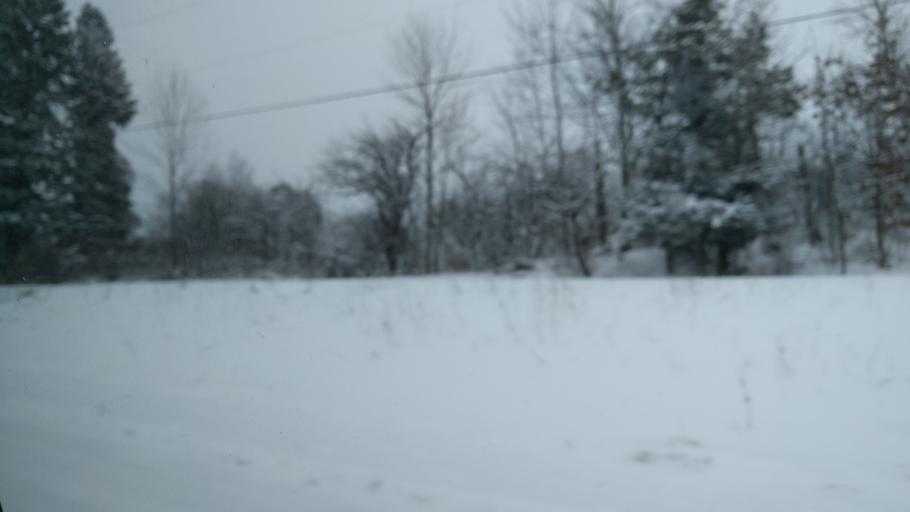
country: US
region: Wisconsin
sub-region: Iron County
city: Hurley
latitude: 46.4242
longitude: -90.2595
